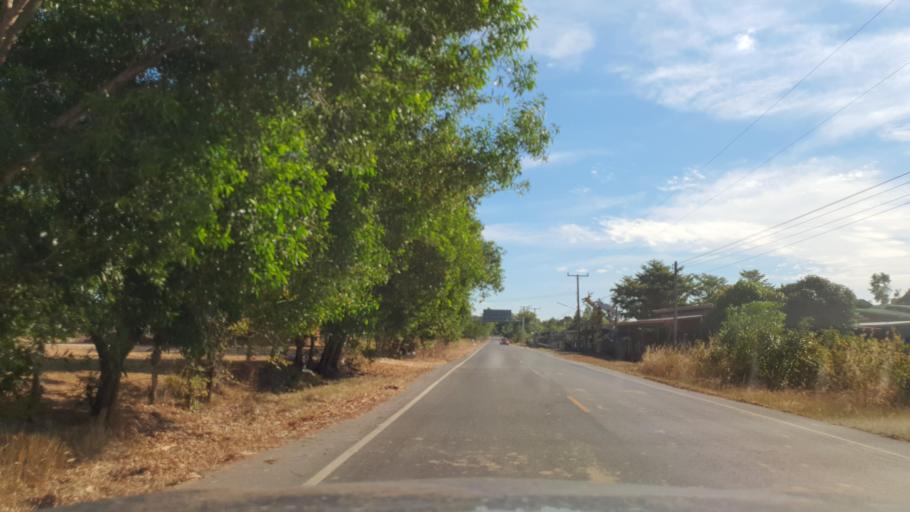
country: TH
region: Kalasin
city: Khao Wong
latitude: 16.6233
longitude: 104.1353
